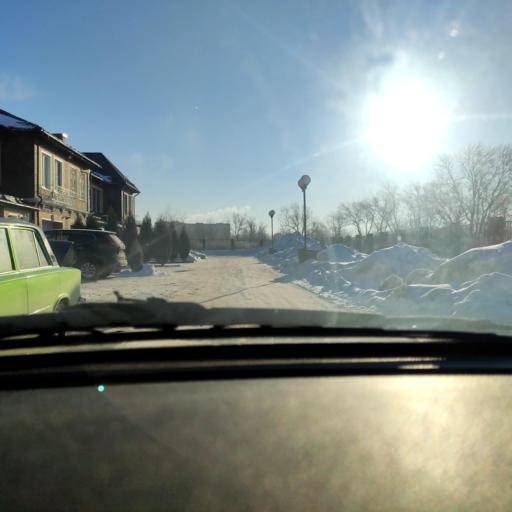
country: RU
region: Samara
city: Tol'yatti
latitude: 53.5041
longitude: 49.2500
